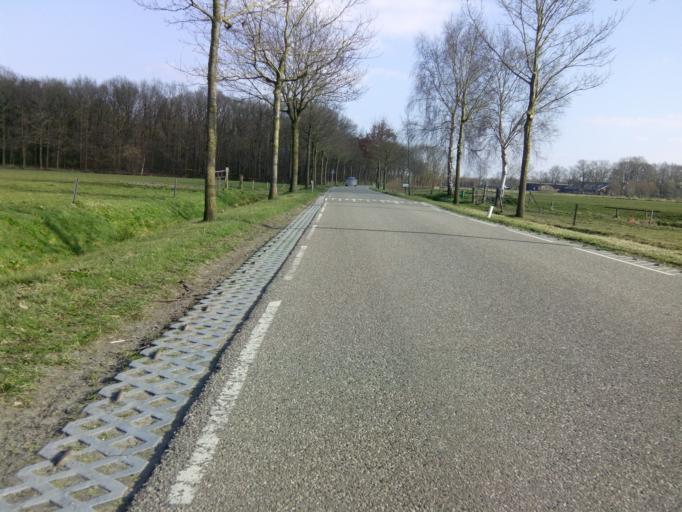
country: NL
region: Utrecht
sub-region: Gemeente Woudenberg
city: Woudenberg
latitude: 52.0888
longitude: 5.4591
